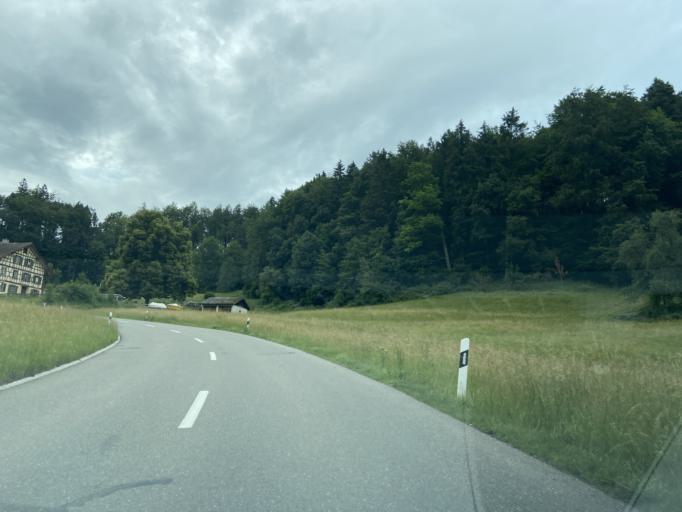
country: CH
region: Thurgau
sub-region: Muenchwilen District
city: Aadorf
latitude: 47.4607
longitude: 8.8963
